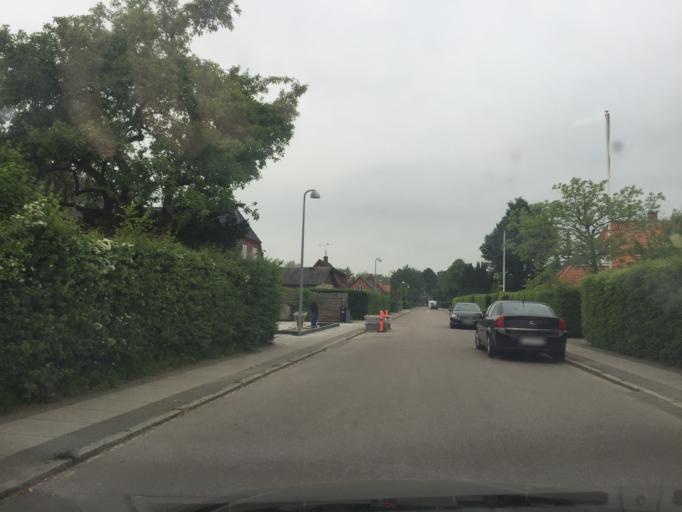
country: DK
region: Capital Region
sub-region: Hoje-Taastrup Kommune
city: Taastrup
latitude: 55.6480
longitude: 12.3049
